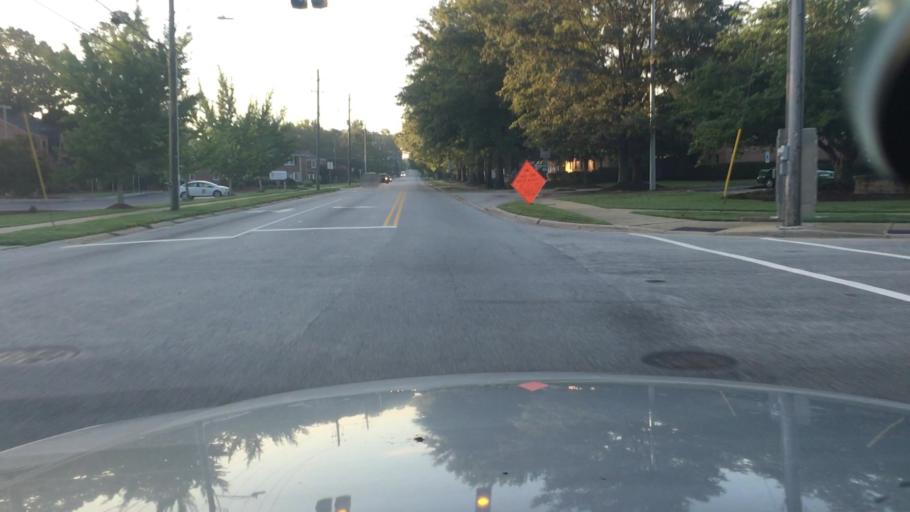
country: US
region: North Carolina
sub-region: Cumberland County
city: Fayetteville
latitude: 35.0696
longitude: -78.9217
